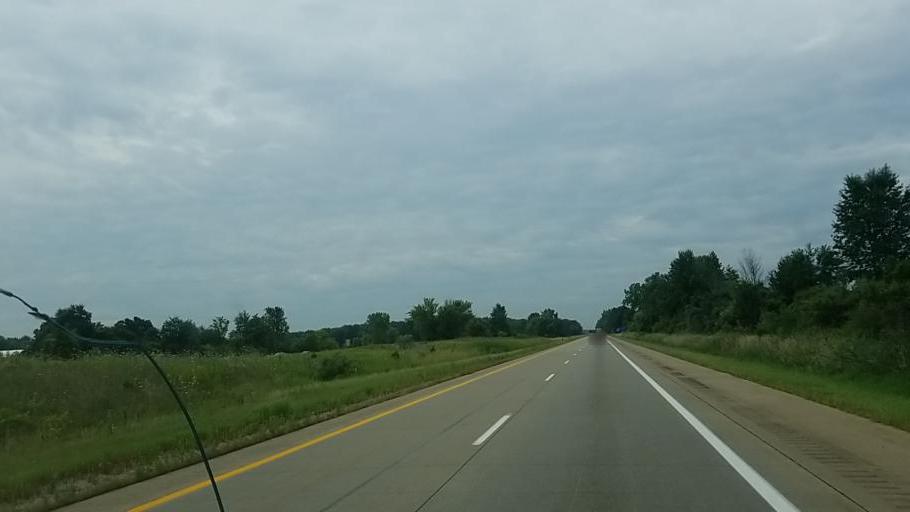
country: US
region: Michigan
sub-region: Branch County
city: Coldwater
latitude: 42.0037
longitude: -84.9726
